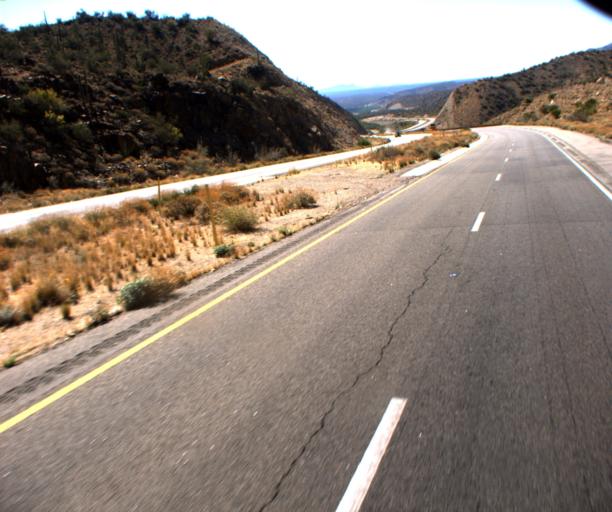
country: US
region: Arizona
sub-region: Yavapai County
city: Bagdad
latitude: 34.4083
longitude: -113.2262
